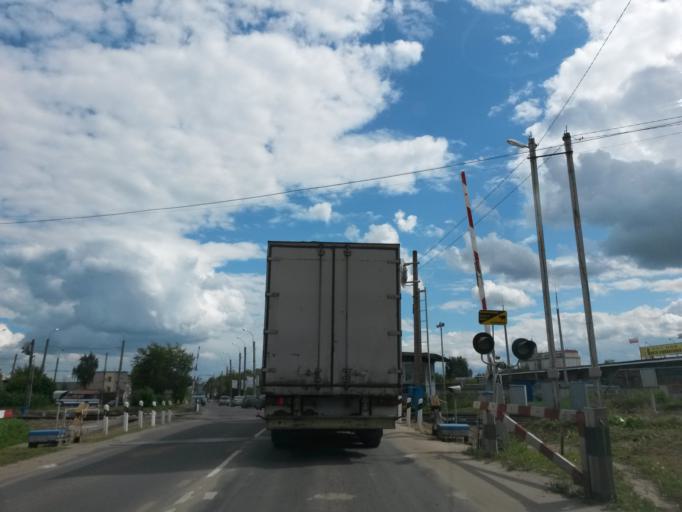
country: RU
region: Ivanovo
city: Novo-Talitsy
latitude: 57.0009
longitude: 40.8974
